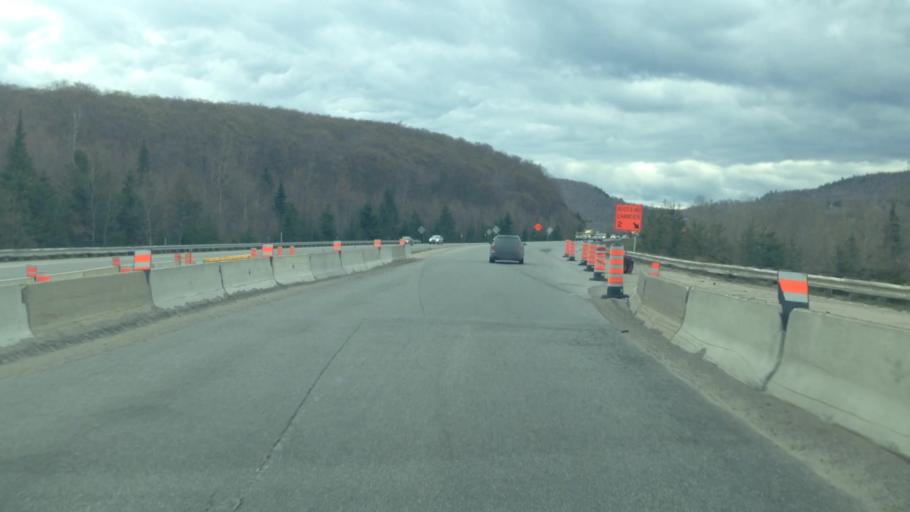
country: CA
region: Quebec
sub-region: Laurentides
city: Sainte-Adele
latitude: 45.9653
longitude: -74.1500
